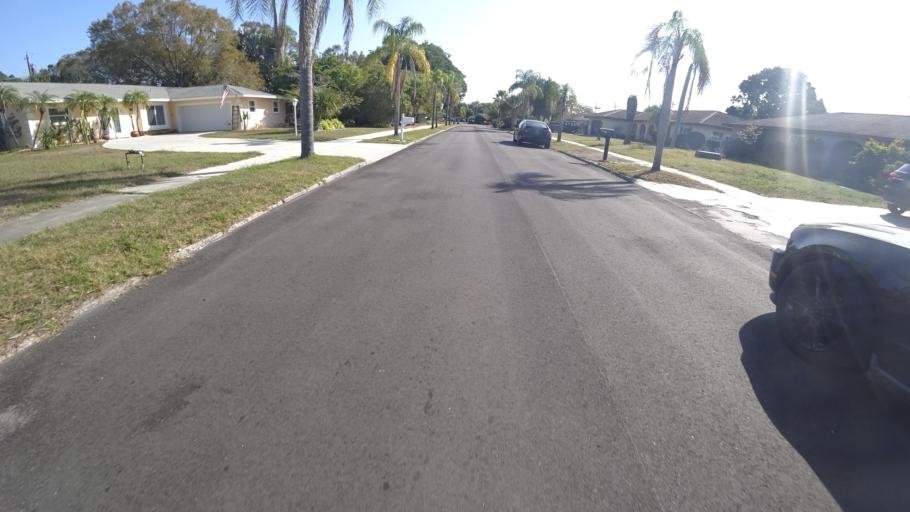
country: US
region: Florida
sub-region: Manatee County
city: Whitfield
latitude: 27.4140
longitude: -82.5688
